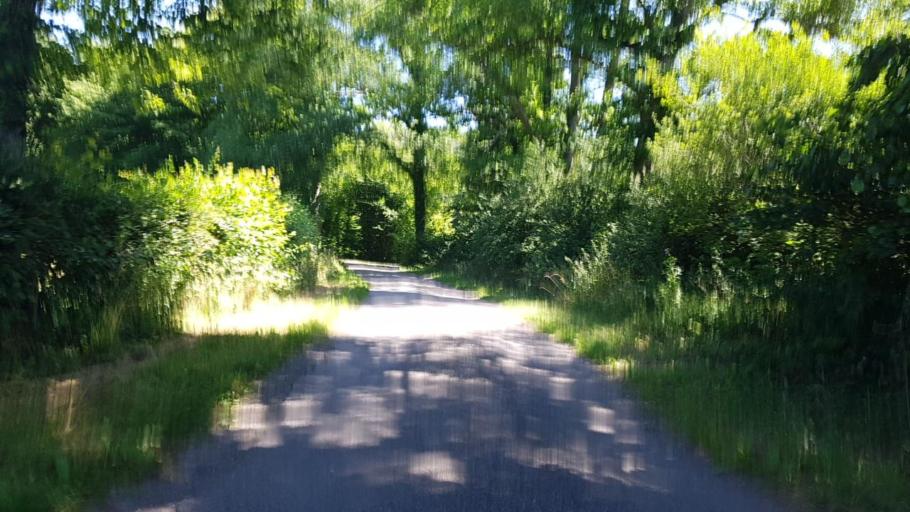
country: BE
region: Wallonia
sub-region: Province du Hainaut
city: Momignies
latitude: 50.0959
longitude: 4.2284
